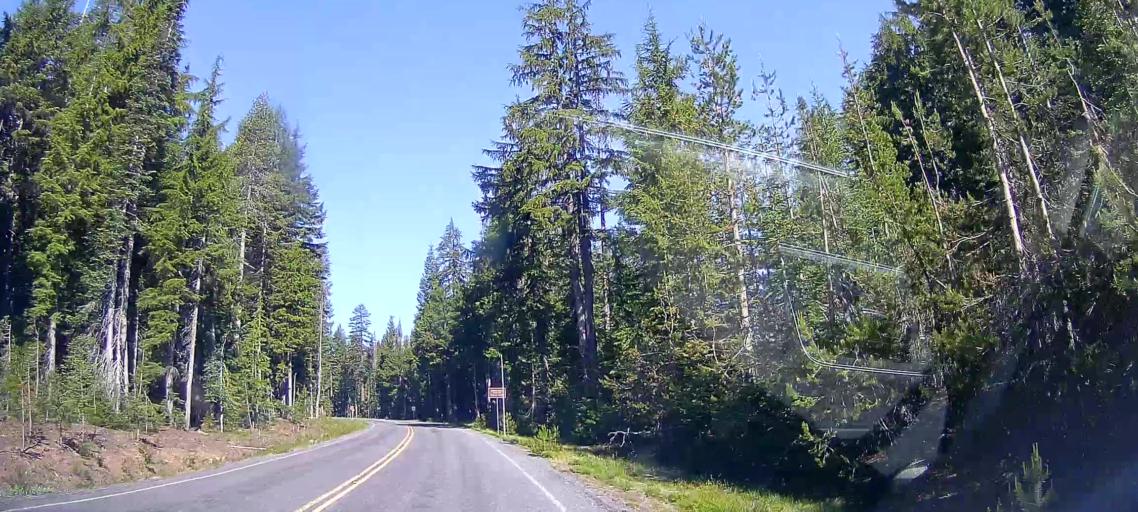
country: US
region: Oregon
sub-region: Jackson County
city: Shady Cove
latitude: 42.8599
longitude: -122.1567
